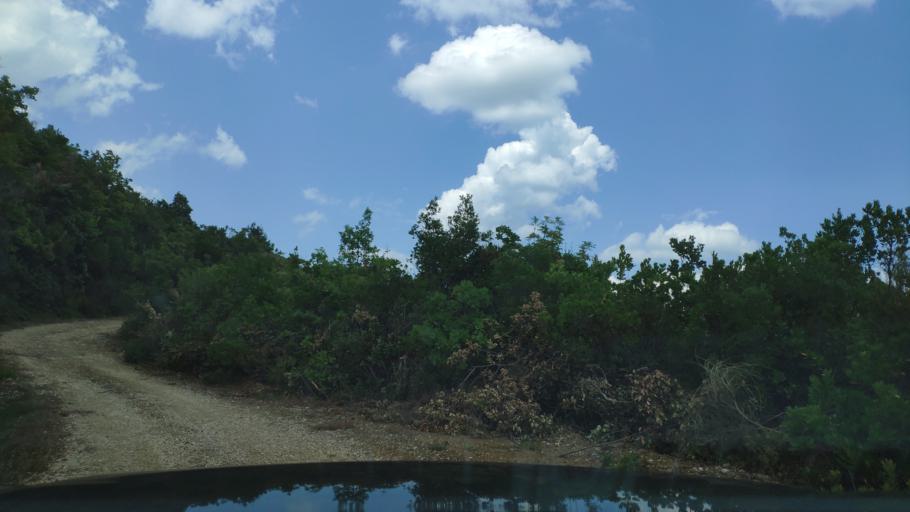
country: GR
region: Epirus
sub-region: Nomos Artas
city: Agios Dimitrios
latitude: 39.3131
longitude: 21.0182
